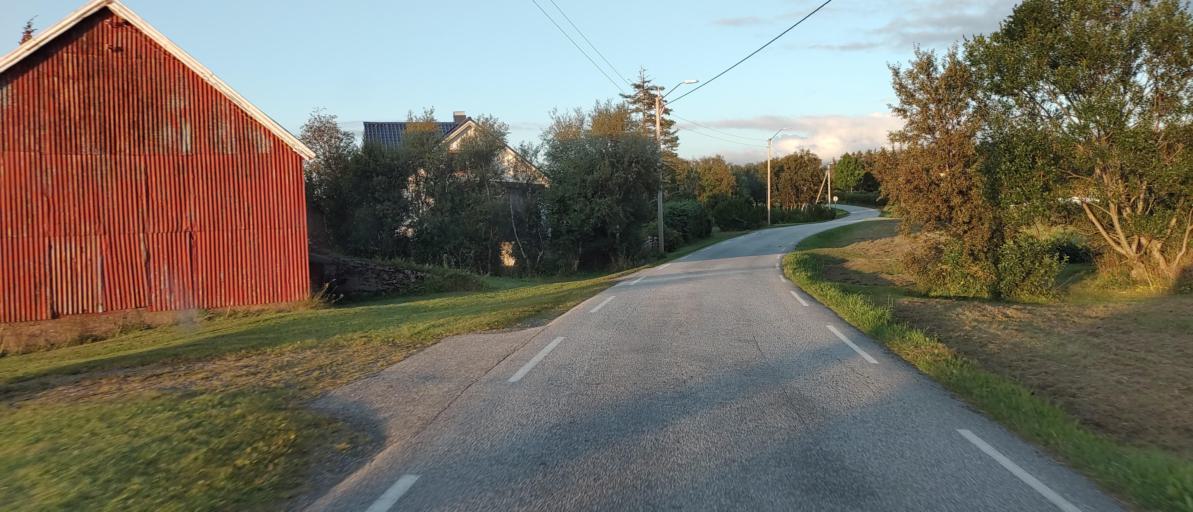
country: NO
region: More og Romsdal
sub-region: Fraena
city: Elnesvagen
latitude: 62.9982
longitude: 7.2277
